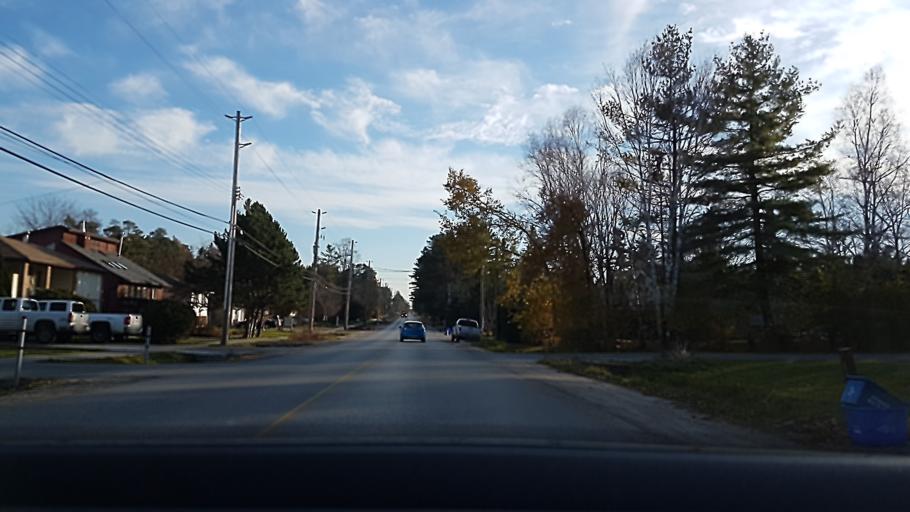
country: CA
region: Ontario
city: Keswick
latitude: 44.3224
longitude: -79.5415
